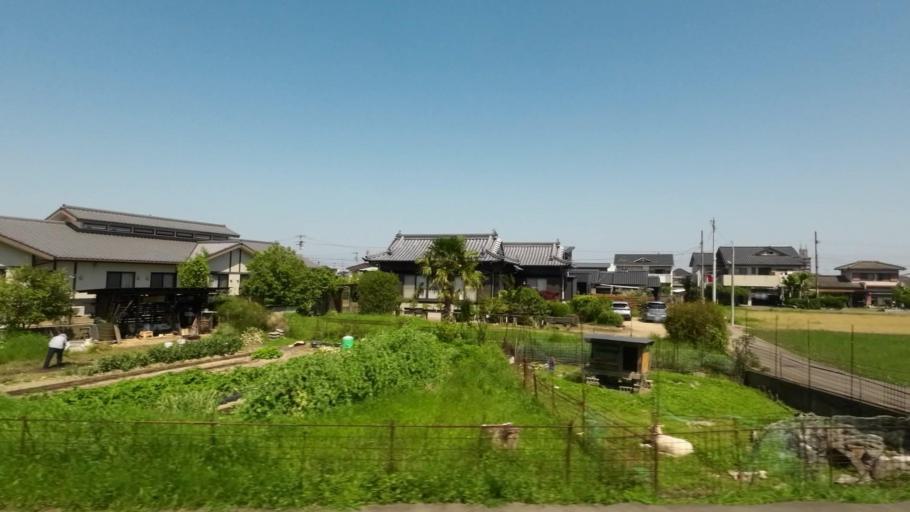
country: JP
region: Ehime
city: Niihama
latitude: 33.9619
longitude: 133.3111
